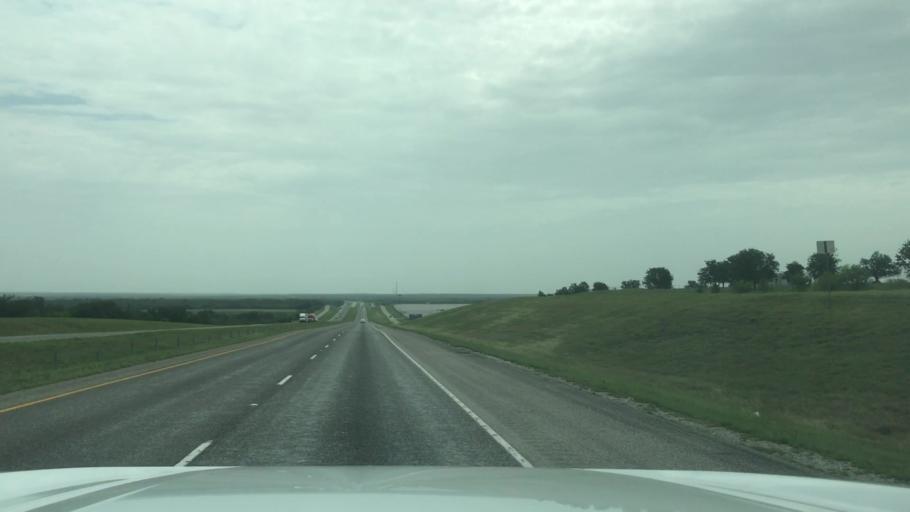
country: US
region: Texas
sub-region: Eastland County
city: Eastland
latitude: 32.3754
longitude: -98.8685
